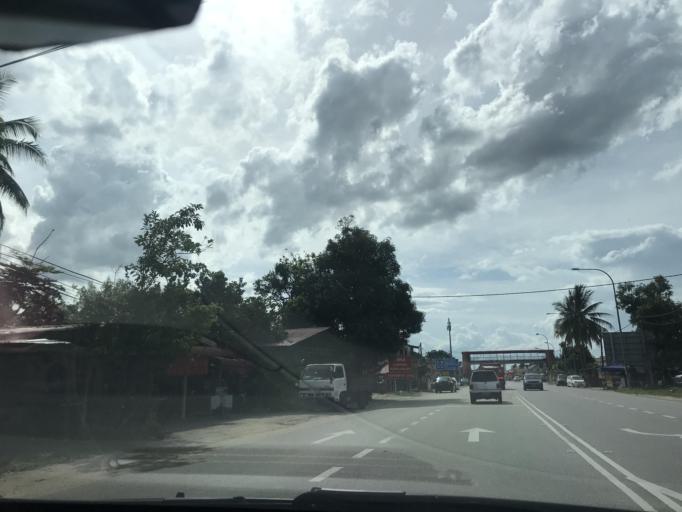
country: MY
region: Kelantan
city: Kampung Lemal
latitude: 6.0229
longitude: 102.1484
